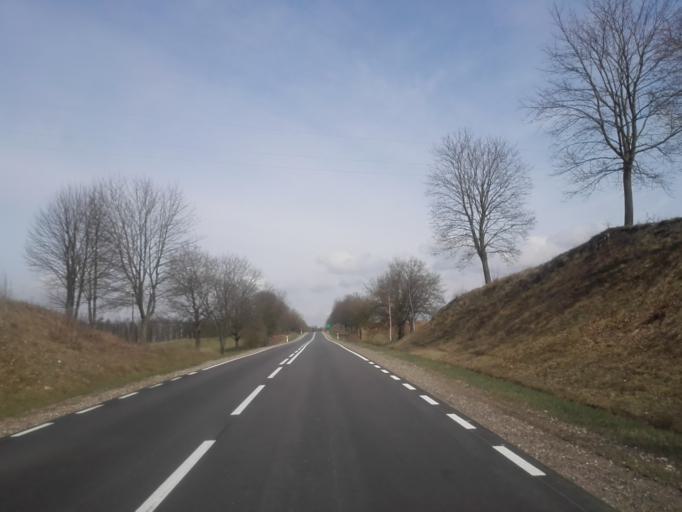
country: PL
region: Podlasie
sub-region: Powiat sejnenski
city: Sejny
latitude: 54.0586
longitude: 23.3568
